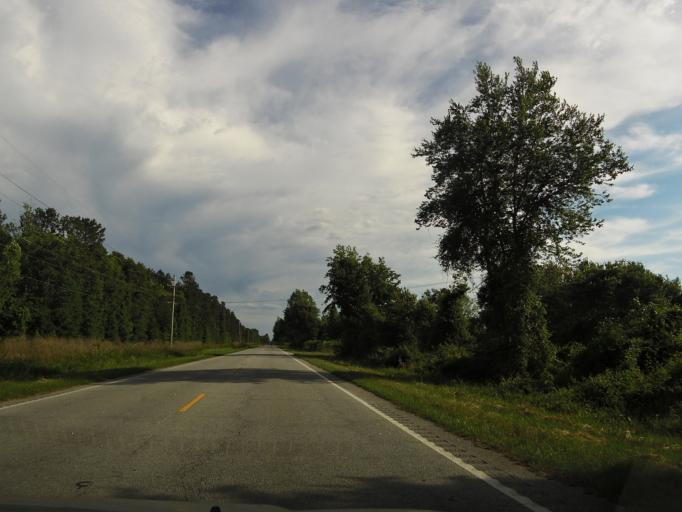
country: US
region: South Carolina
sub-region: Hampton County
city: Estill
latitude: 32.8262
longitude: -81.2396
